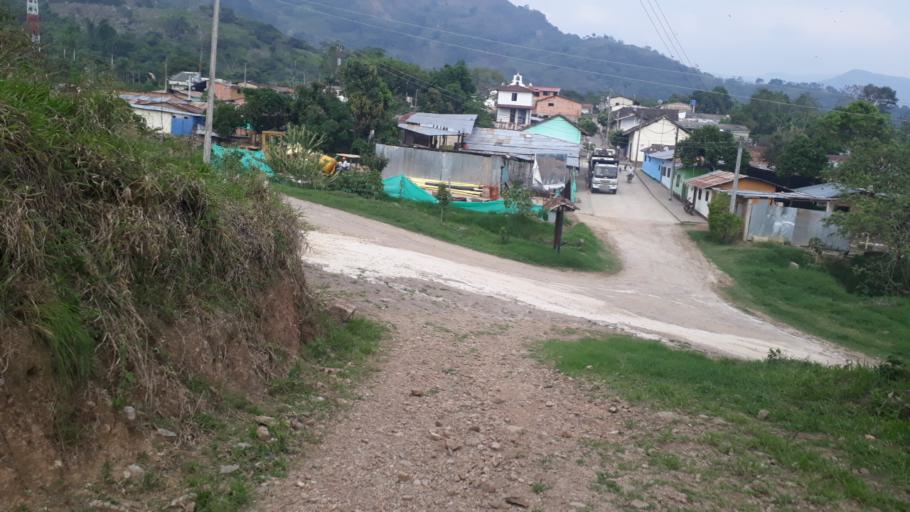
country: CO
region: Casanare
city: Nunchia
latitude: 5.6249
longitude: -72.4253
